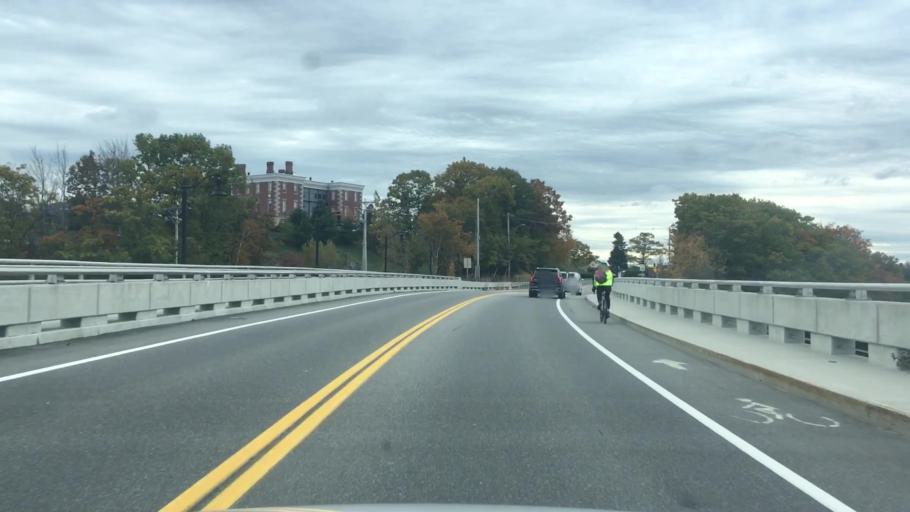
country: US
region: Maine
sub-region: Cumberland County
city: Portland
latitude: 43.6903
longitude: -70.2458
